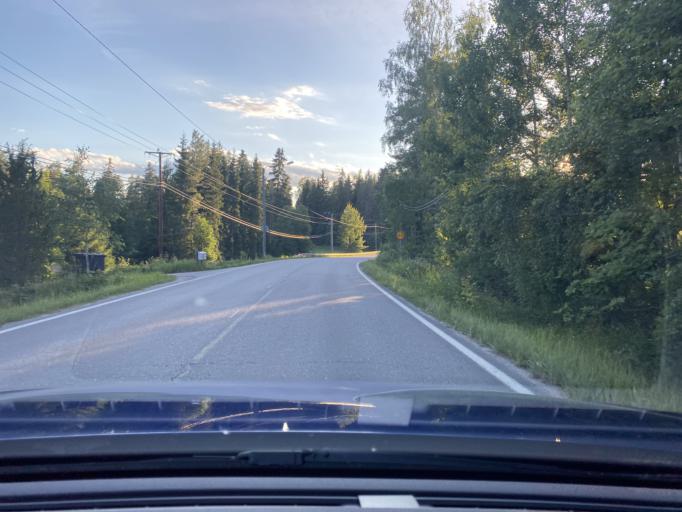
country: FI
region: Uusimaa
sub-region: Helsinki
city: Nurmijaervi
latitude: 60.4056
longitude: 24.7885
